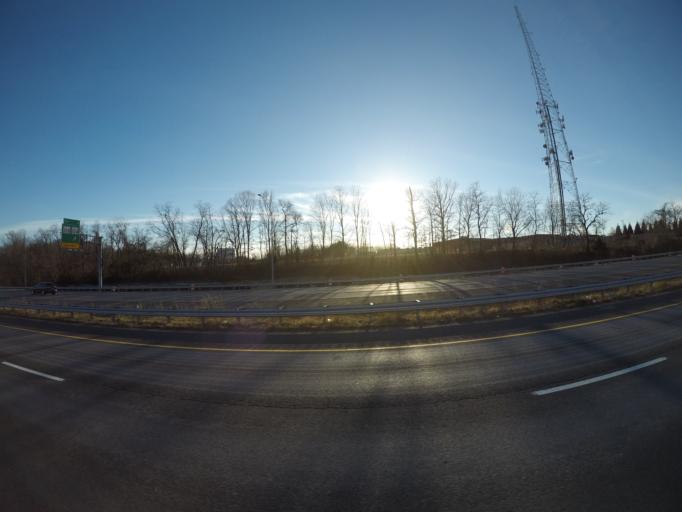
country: US
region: Maryland
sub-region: Howard County
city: Columbia
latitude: 39.2266
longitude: -76.8088
